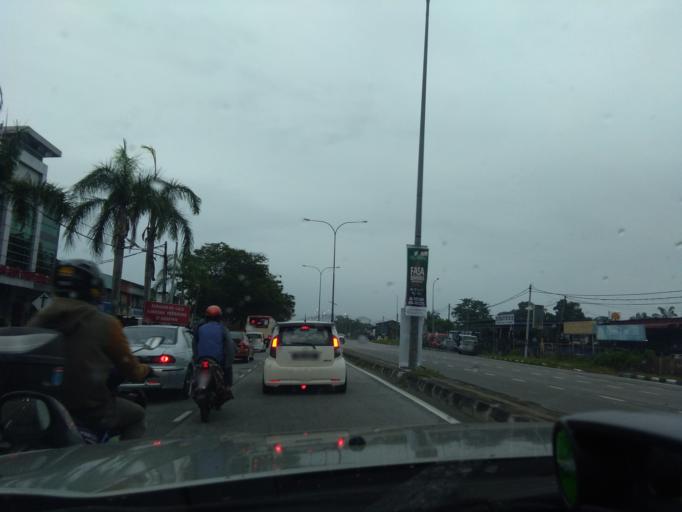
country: MY
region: Penang
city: Nibong Tebal
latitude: 5.1823
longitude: 100.4849
